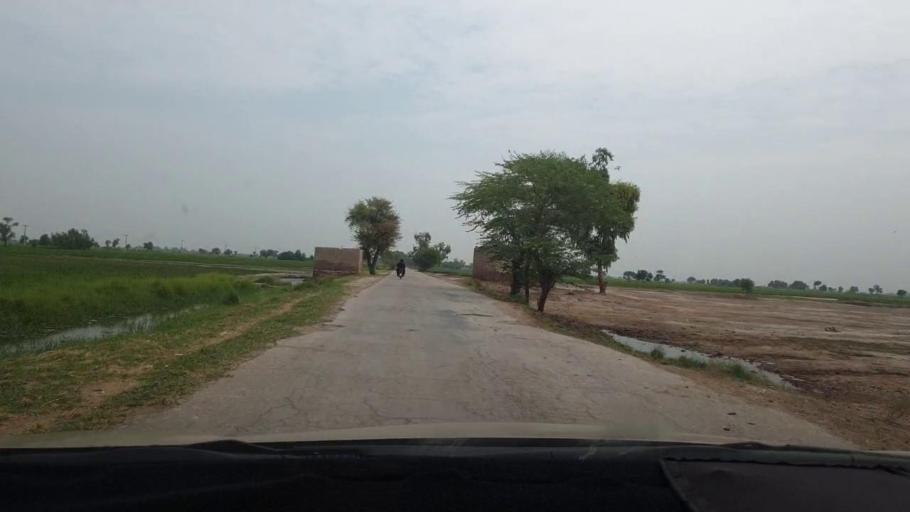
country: PK
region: Sindh
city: Ratodero
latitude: 27.7526
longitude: 68.3176
